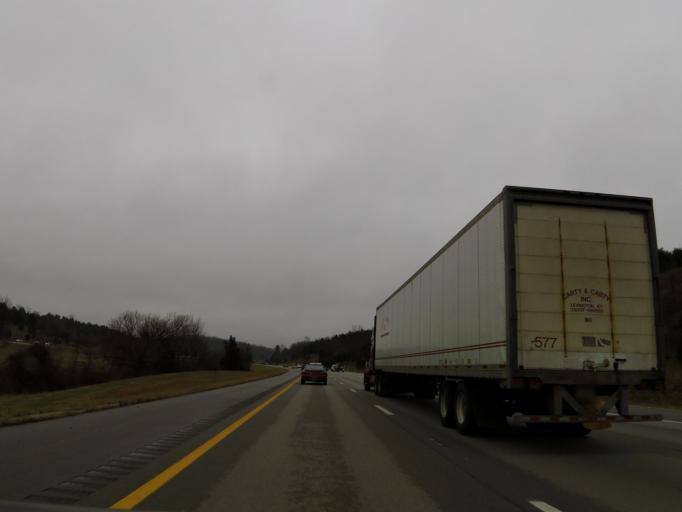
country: US
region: Kentucky
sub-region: Scott County
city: Georgetown
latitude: 38.3387
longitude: -84.5679
